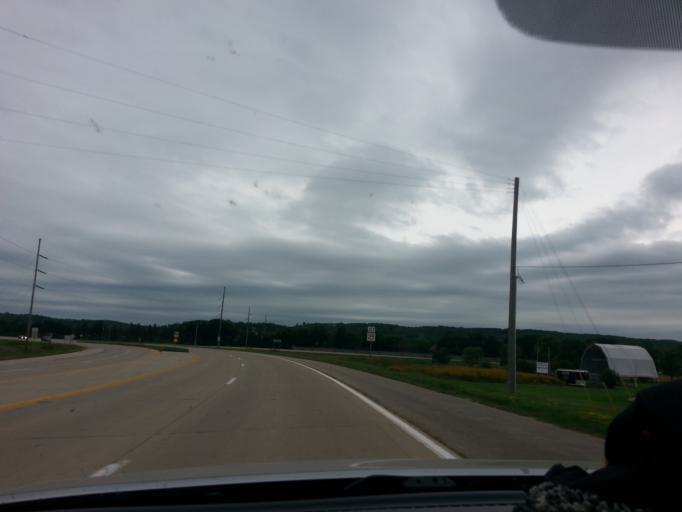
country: US
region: Minnesota
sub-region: Olmsted County
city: Rochester
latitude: 44.0061
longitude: -92.5089
